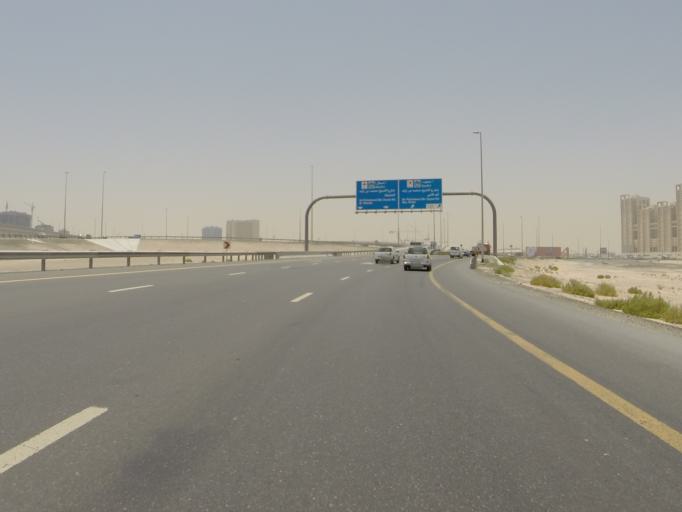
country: AE
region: Dubai
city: Dubai
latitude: 25.0461
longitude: 55.1973
